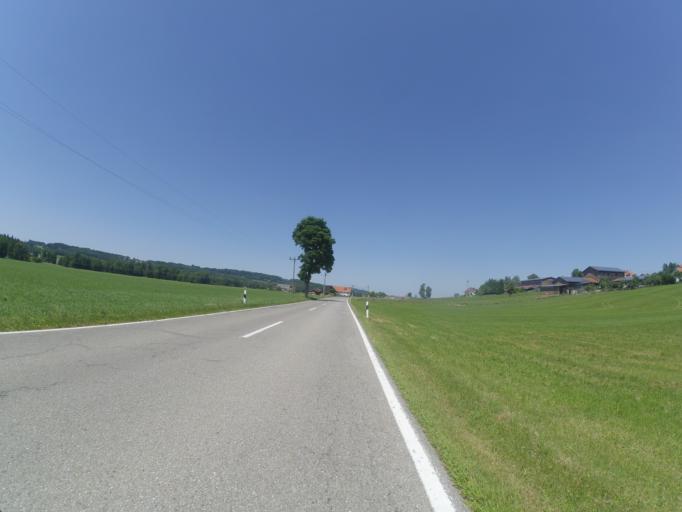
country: DE
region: Bavaria
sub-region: Swabia
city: Bohen
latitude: 47.9083
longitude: 10.3118
